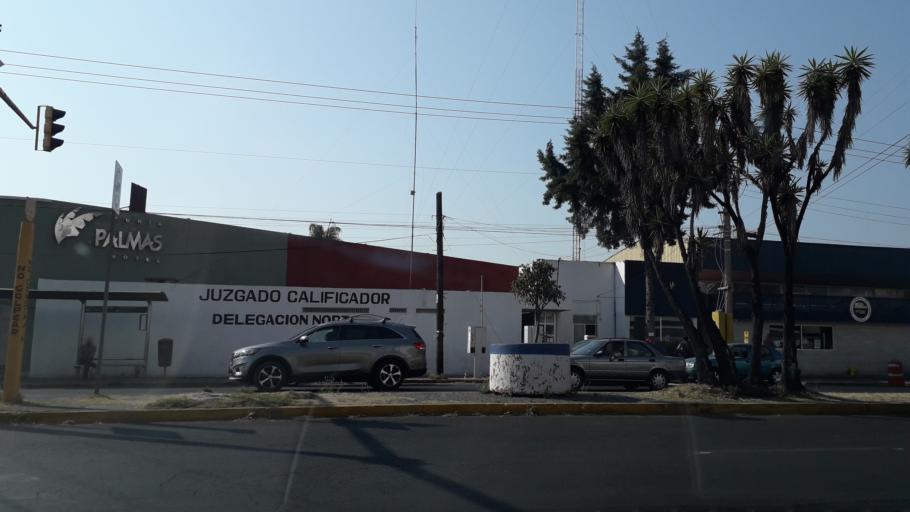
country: MX
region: Puebla
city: Puebla
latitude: 19.0568
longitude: -98.2131
